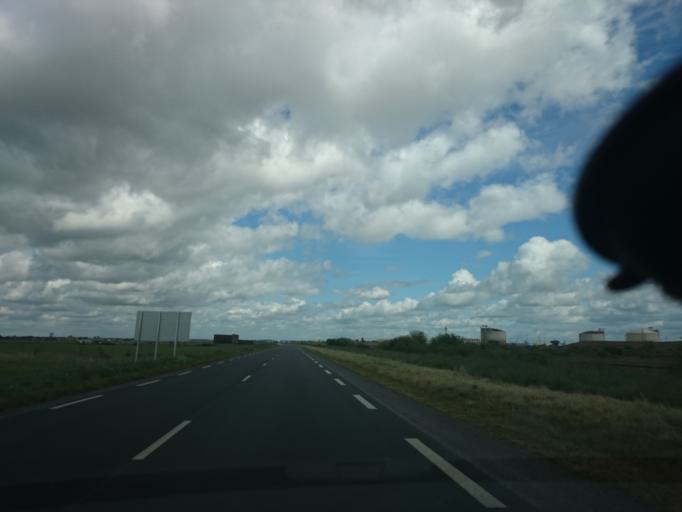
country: FR
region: Pays de la Loire
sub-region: Departement de la Loire-Atlantique
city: Trignac
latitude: 47.3036
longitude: -2.1651
